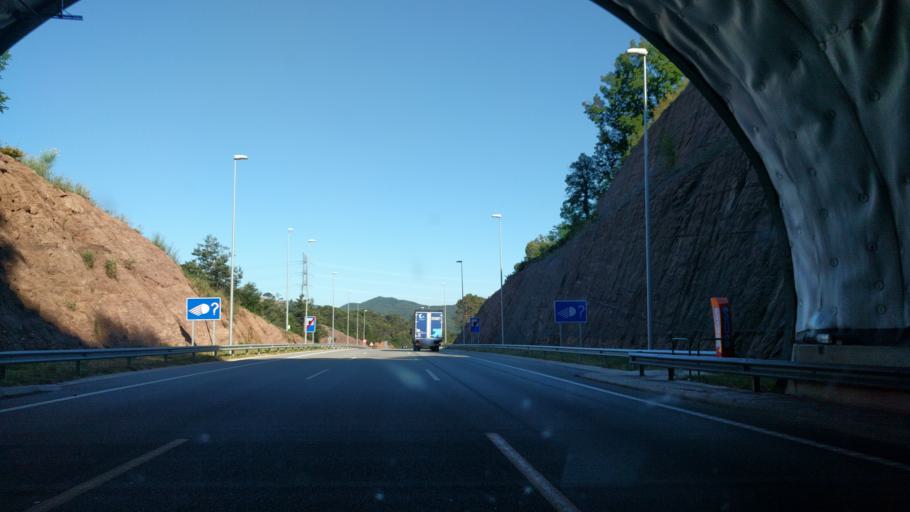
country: ES
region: Catalonia
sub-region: Provincia de Barcelona
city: Sant Julia de Vilatorta
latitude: 41.9010
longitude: 2.3388
